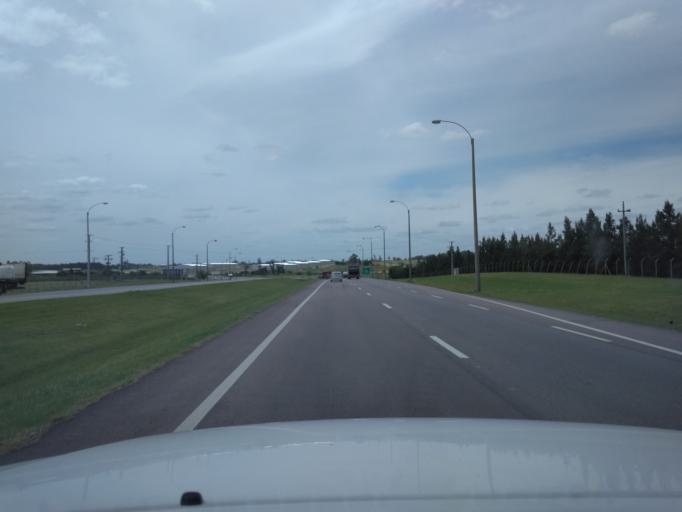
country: UY
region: Canelones
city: Las Piedras
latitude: -34.6987
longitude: -56.2389
